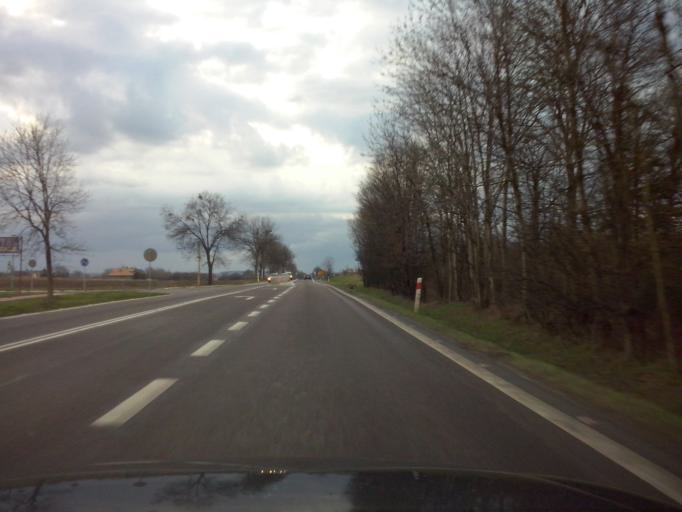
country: PL
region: Lublin Voivodeship
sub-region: Chelm
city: Chelm
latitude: 51.1585
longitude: 23.4006
